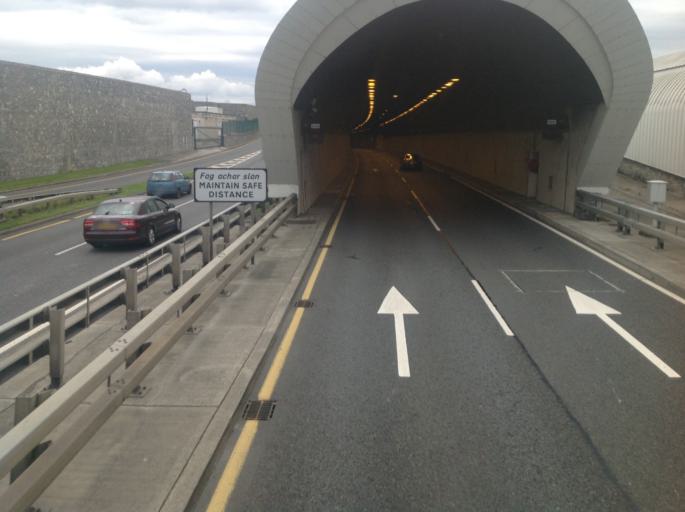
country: IE
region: Leinster
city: Beaumont
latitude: 53.3959
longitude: -6.2396
